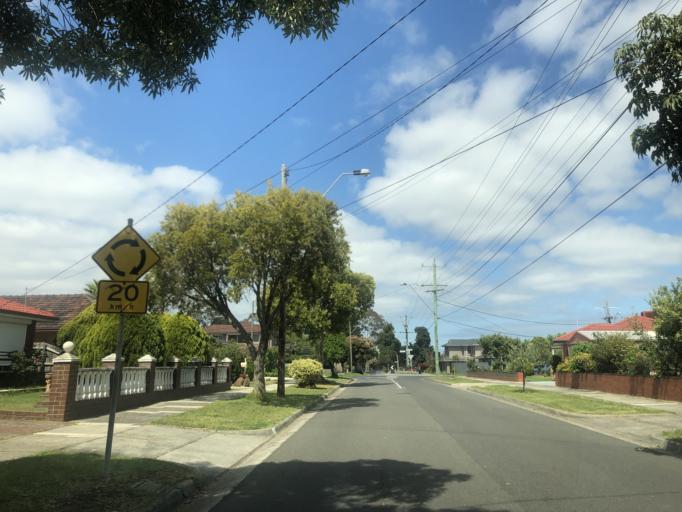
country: AU
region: Victoria
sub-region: Greater Dandenong
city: Springvale
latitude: -37.9226
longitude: 145.1691
